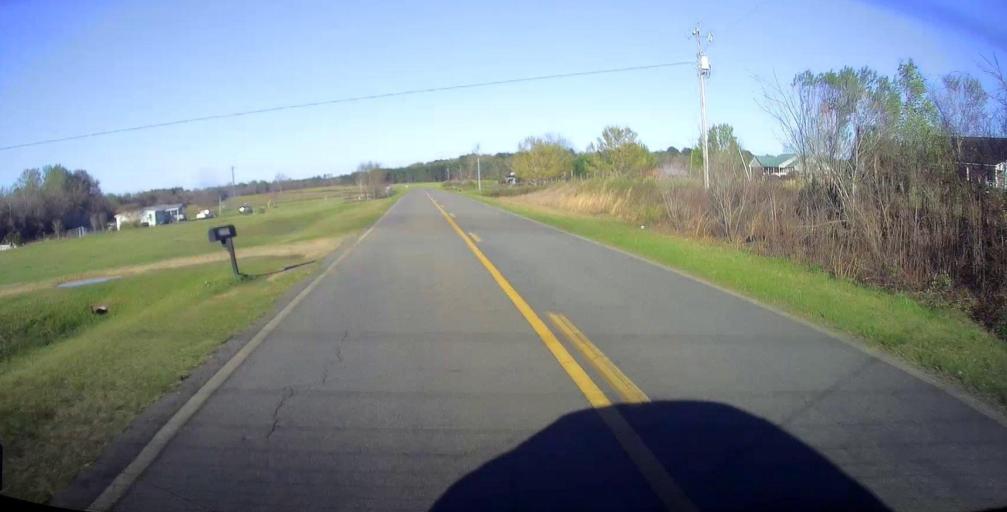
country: US
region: Georgia
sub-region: Pulaski County
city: Hawkinsville
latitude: 32.3135
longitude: -83.5759
